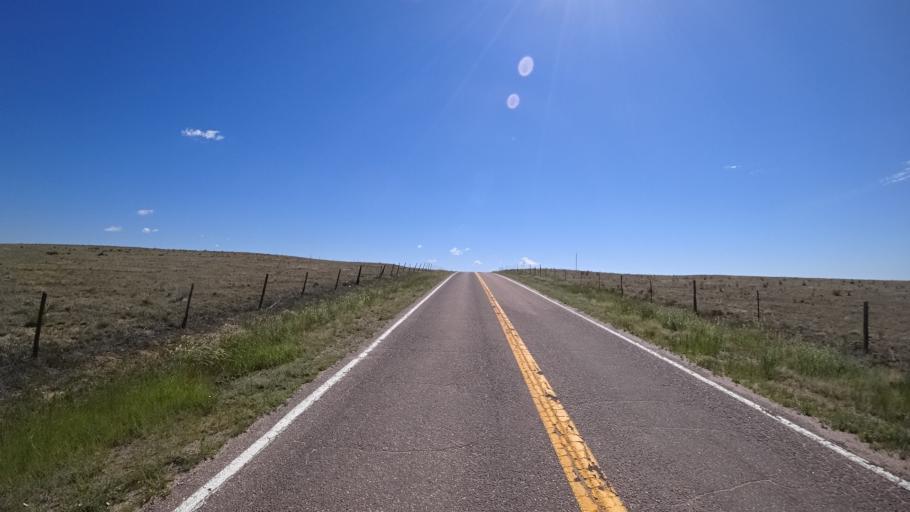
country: US
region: Colorado
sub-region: El Paso County
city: Security-Widefield
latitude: 38.7810
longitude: -104.6228
